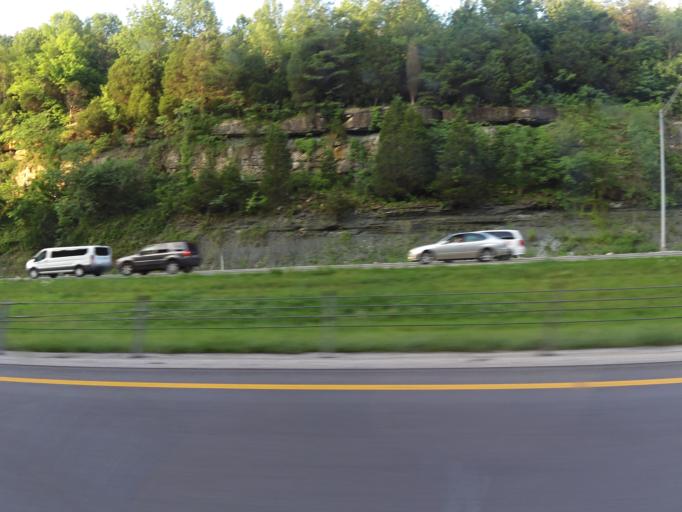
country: US
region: Kentucky
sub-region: Rockcastle County
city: Mount Vernon
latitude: 37.3818
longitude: -84.3345
